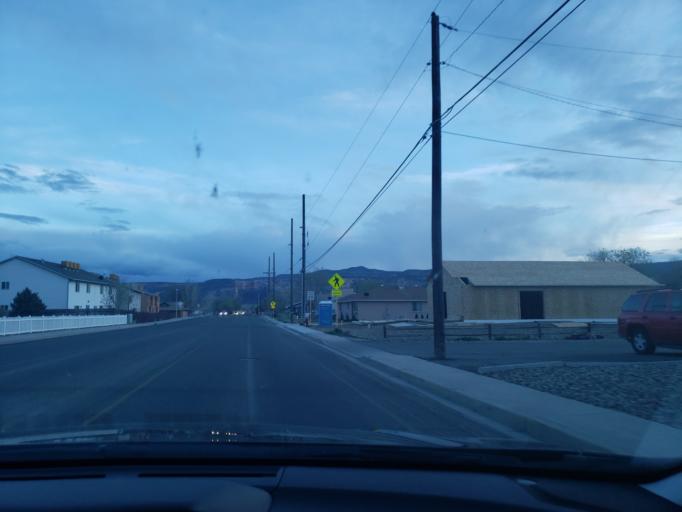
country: US
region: Colorado
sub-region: Mesa County
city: Fruita
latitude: 39.1576
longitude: -108.7198
